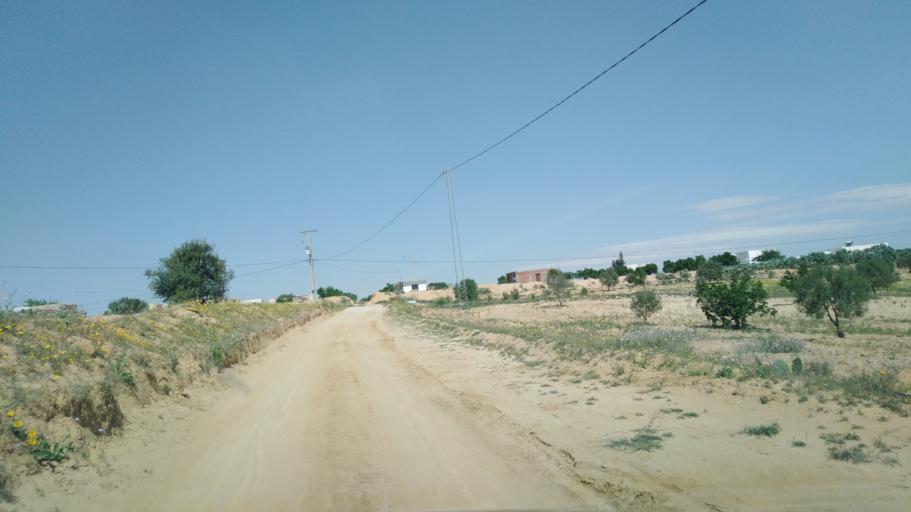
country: TN
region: Safaqis
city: Sfax
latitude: 34.7777
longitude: 10.5251
